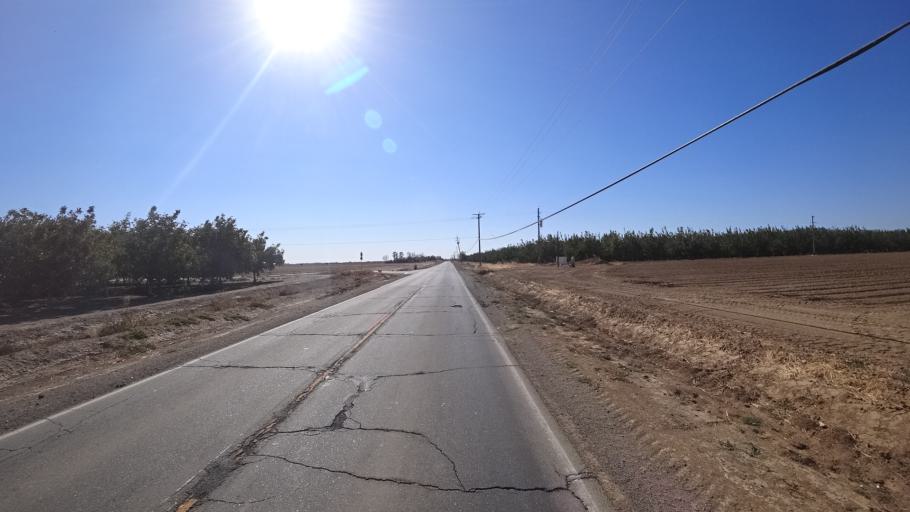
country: US
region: California
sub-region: Yolo County
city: Winters
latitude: 38.5624
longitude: -121.9713
